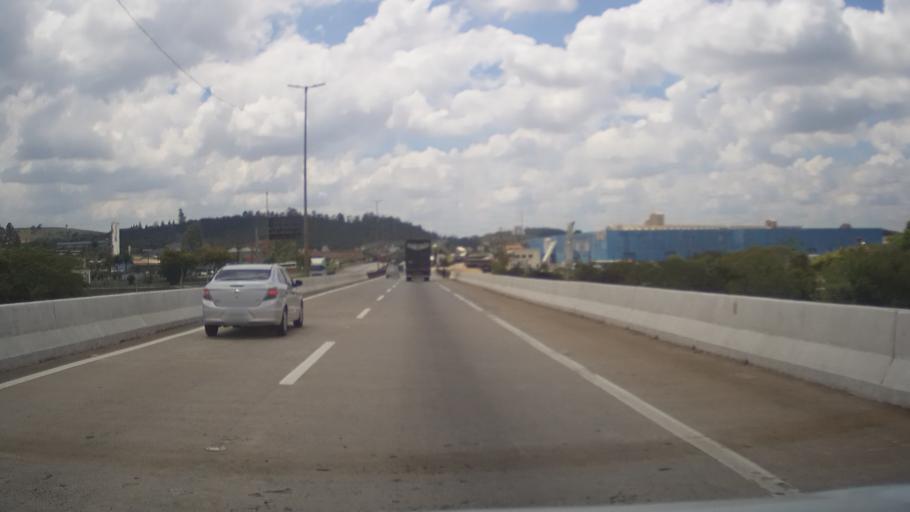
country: BR
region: Minas Gerais
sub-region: Tres Coracoes
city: Tres Coracoes
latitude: -21.6720
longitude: -45.3332
